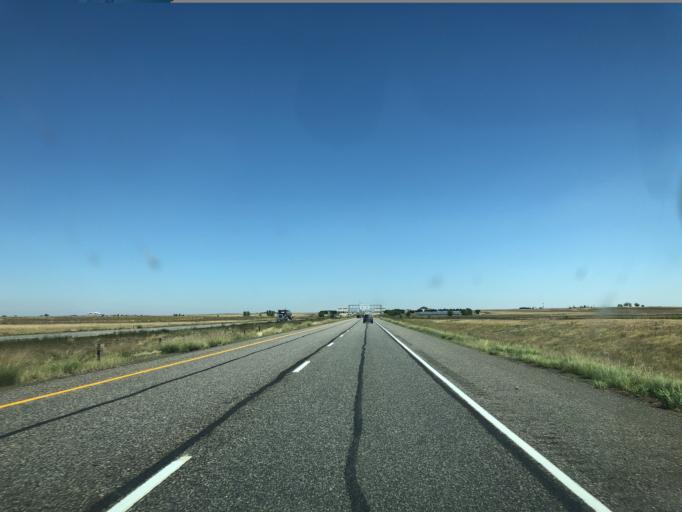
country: US
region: Colorado
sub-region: Adams County
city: Aurora
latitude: 39.7601
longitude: -104.7165
